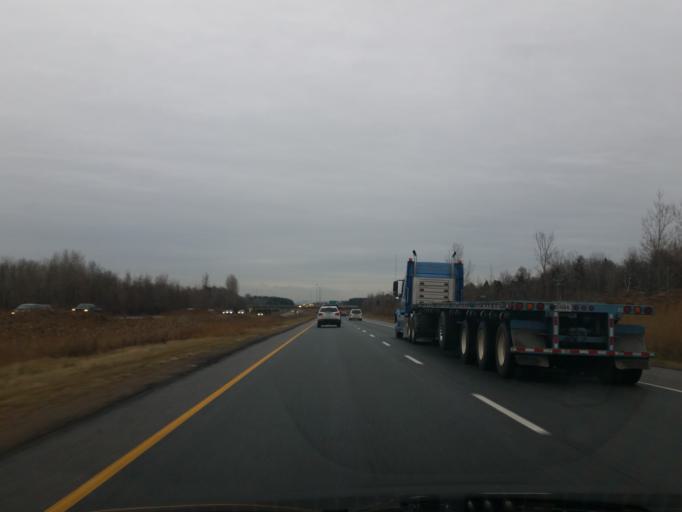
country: CA
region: Quebec
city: L'Ancienne-Lorette
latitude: 46.7595
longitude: -71.3904
